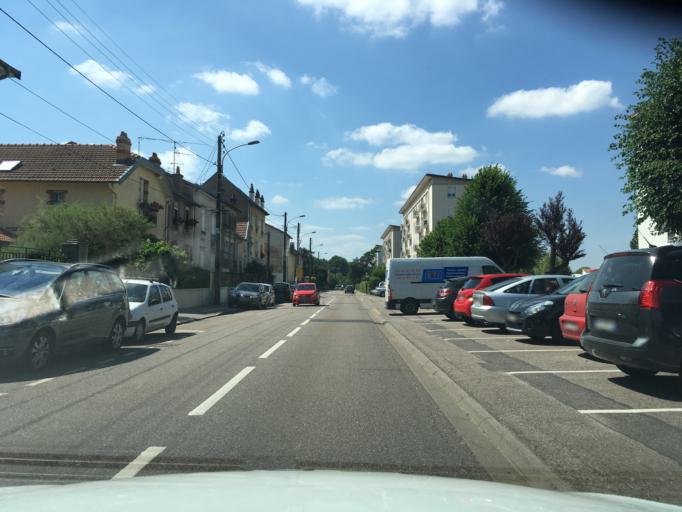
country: FR
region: Lorraine
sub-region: Departement de Meurthe-et-Moselle
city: Jarville-la-Malgrange
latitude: 48.6697
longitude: 6.1980
